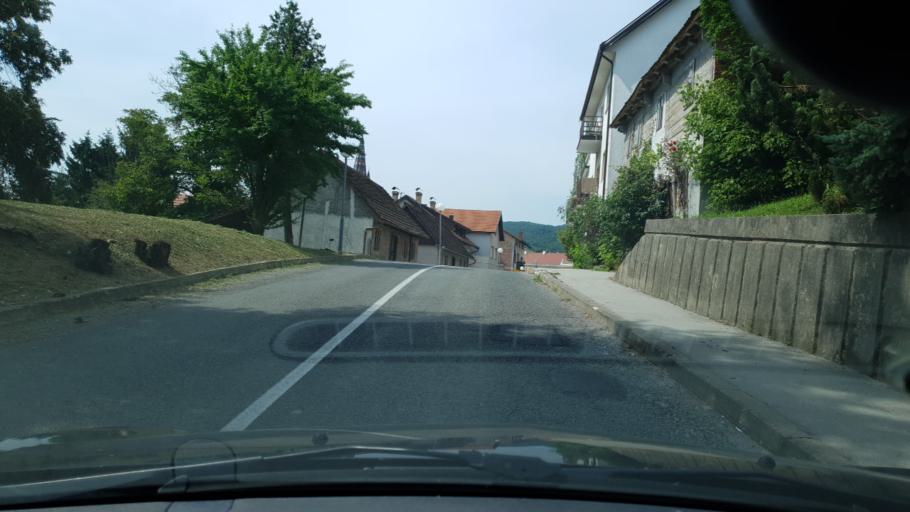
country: HR
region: Krapinsko-Zagorska
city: Marija Bistrica
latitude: 46.0065
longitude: 16.1210
